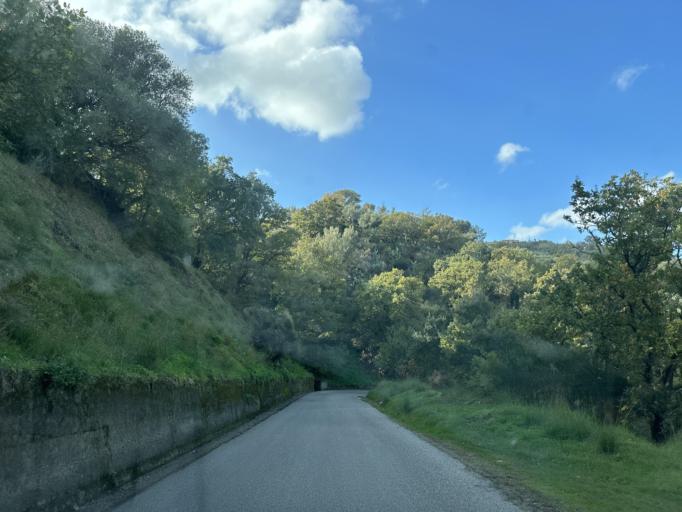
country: IT
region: Calabria
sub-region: Provincia di Catanzaro
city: Montepaone
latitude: 38.7185
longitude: 16.5081
